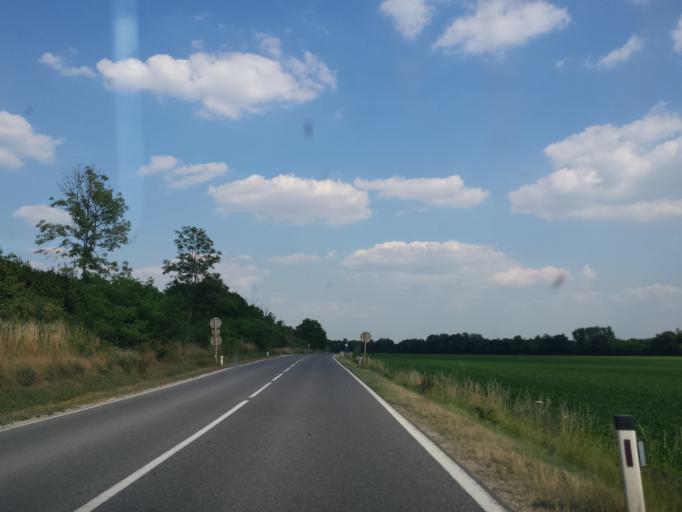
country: AT
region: Lower Austria
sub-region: Politischer Bezirk Ganserndorf
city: Parbasdorf
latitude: 48.2799
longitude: 16.5962
